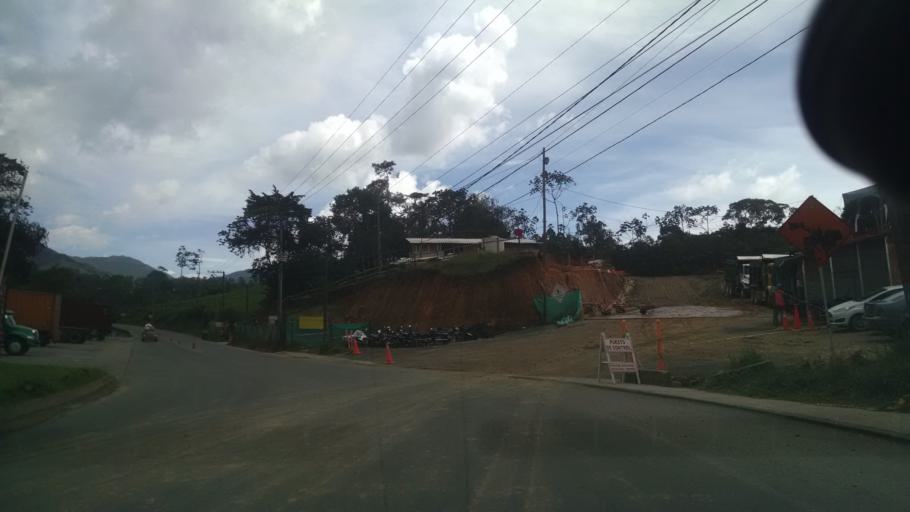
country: CO
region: Antioquia
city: Caldas
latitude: 6.0580
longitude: -75.6302
